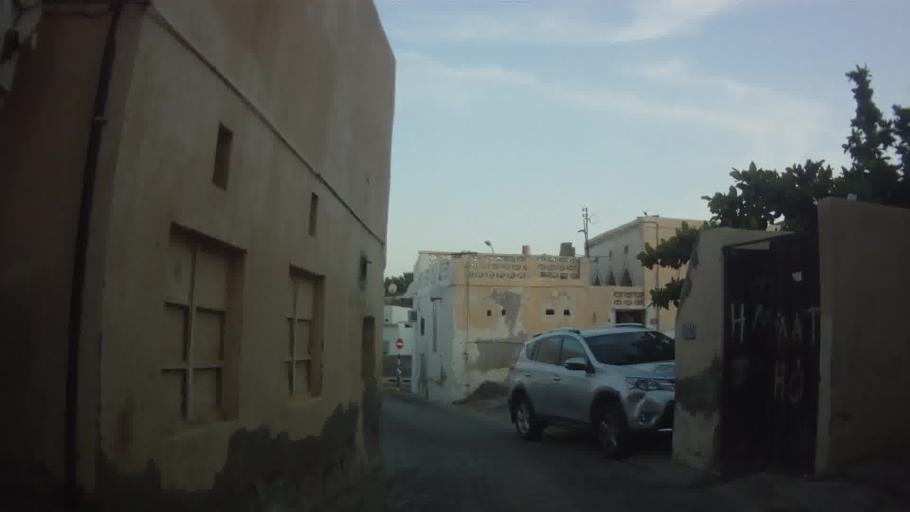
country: OM
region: Muhafazat Masqat
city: Muscat
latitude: 23.6170
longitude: 58.5881
